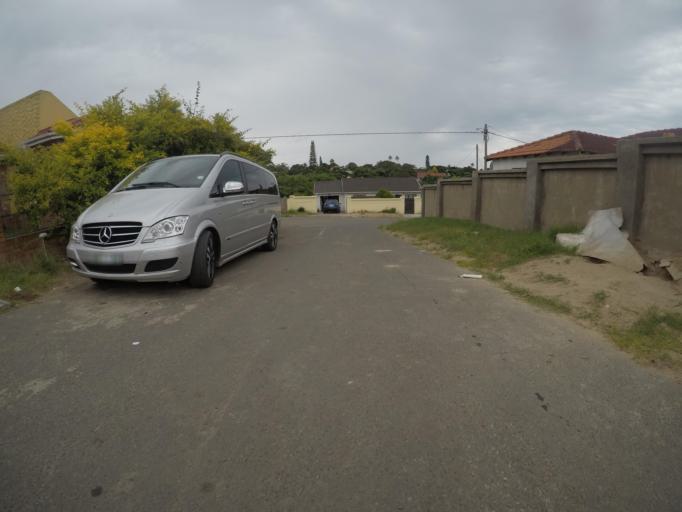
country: ZA
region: Eastern Cape
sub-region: Buffalo City Metropolitan Municipality
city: East London
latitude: -32.9949
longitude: 27.8470
